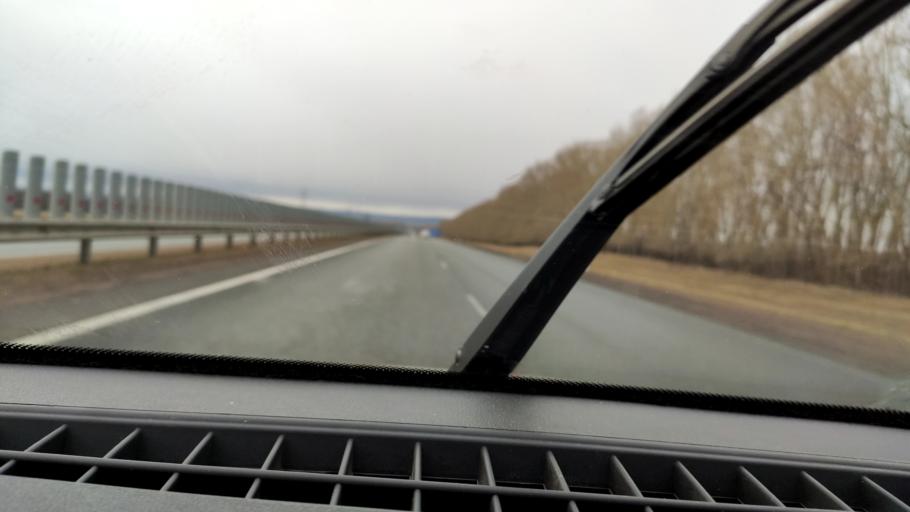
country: RU
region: Bashkortostan
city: Kushnarenkovo
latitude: 55.0490
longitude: 55.4423
